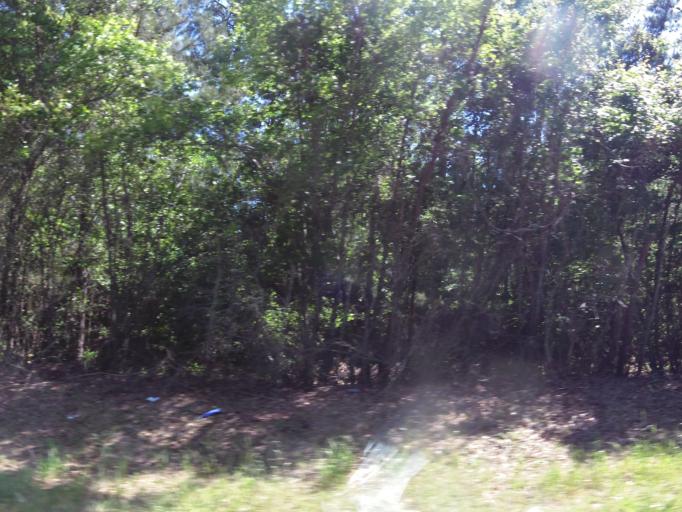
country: US
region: South Carolina
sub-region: Aiken County
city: New Ellenton
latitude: 33.5162
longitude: -81.5855
